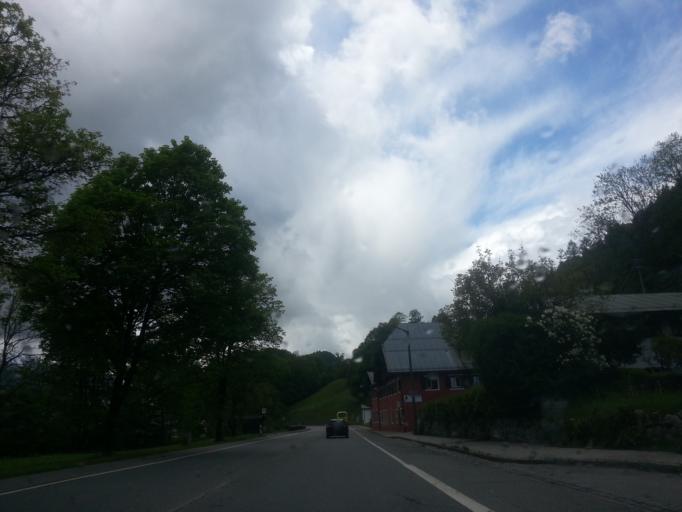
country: DE
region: Bavaria
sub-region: Upper Bavaria
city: Berchtesgaden
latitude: 47.6423
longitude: 13.0199
